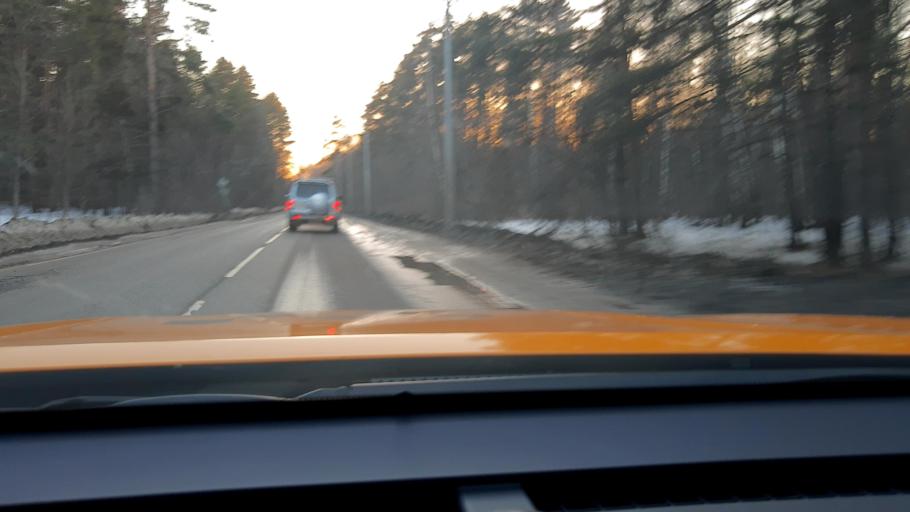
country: RU
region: Moskovskaya
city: Petrovskaya
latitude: 55.5323
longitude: 37.7645
